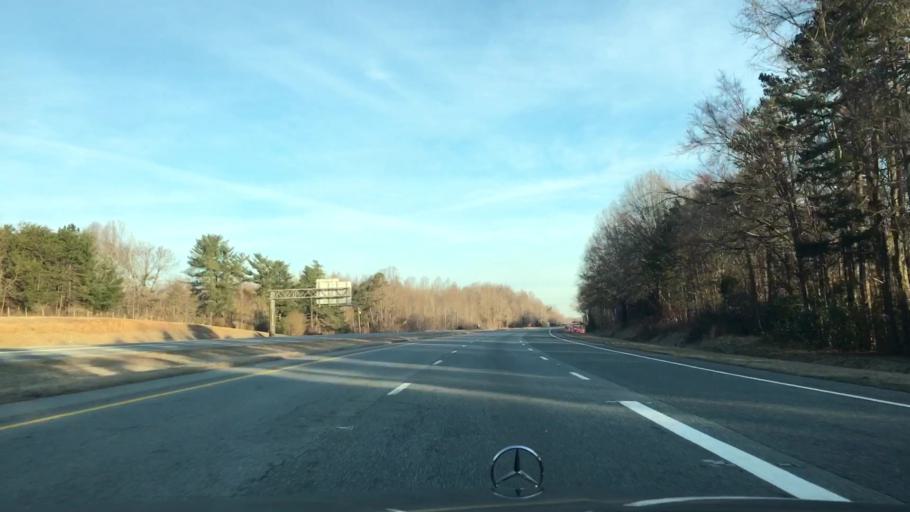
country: US
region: North Carolina
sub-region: Guilford County
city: Pleasant Garden
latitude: 36.0035
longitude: -79.7563
